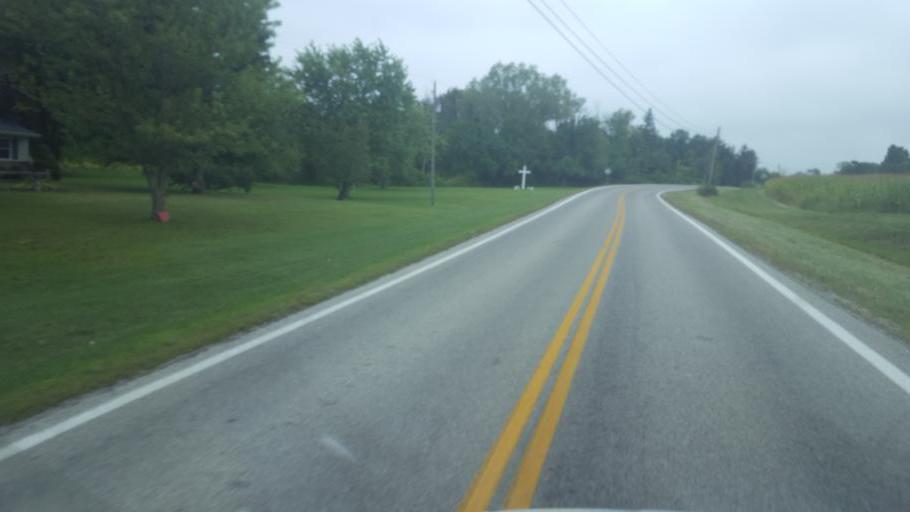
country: US
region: Ohio
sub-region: Knox County
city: Centerburg
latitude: 40.3485
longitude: -82.6902
